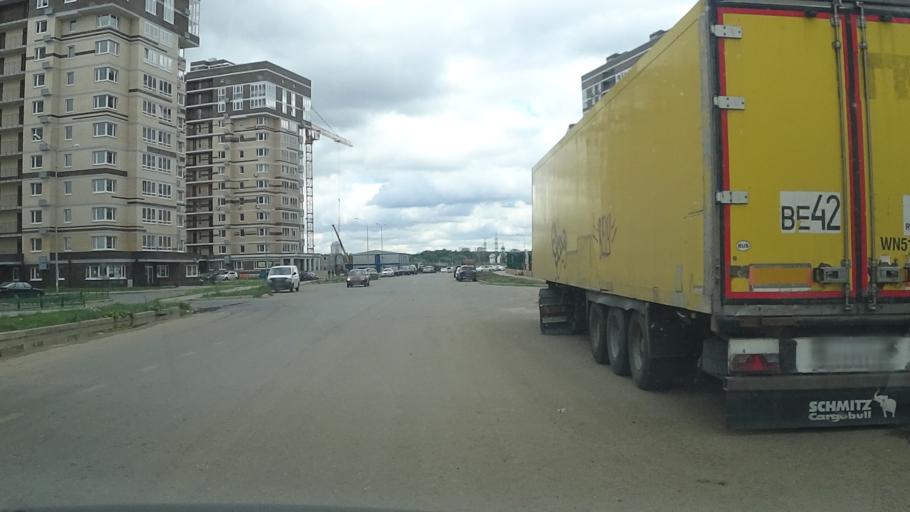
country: RU
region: Moscow
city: Mikhalkovo
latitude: 55.6576
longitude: 37.4224
